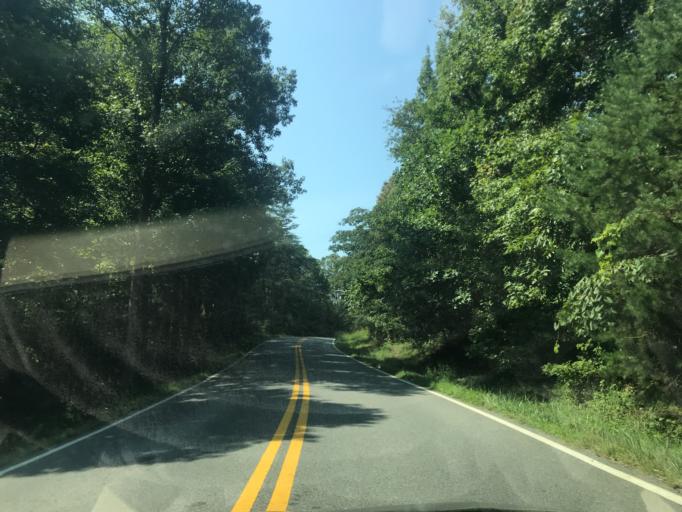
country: US
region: Maryland
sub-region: Calvert County
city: Prince Frederick
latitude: 38.4932
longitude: -76.6066
